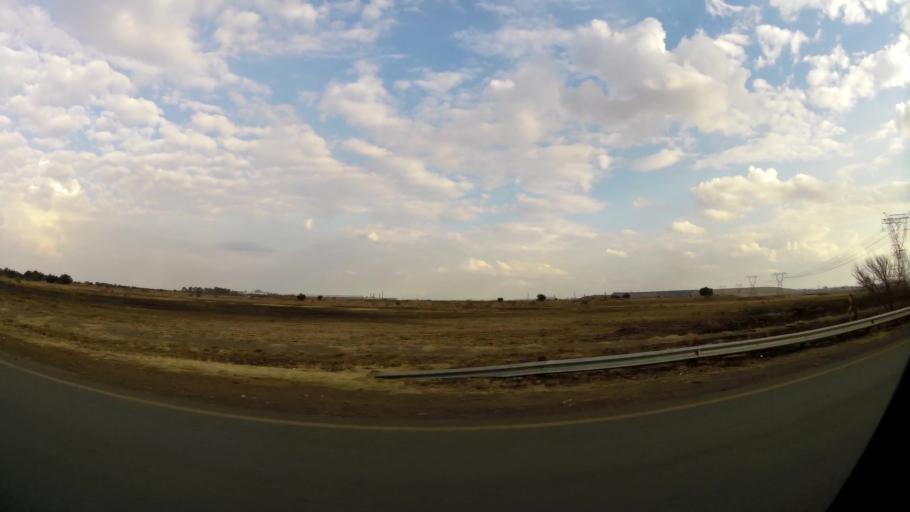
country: ZA
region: Gauteng
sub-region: Sedibeng District Municipality
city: Vanderbijlpark
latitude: -26.6191
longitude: 27.8294
